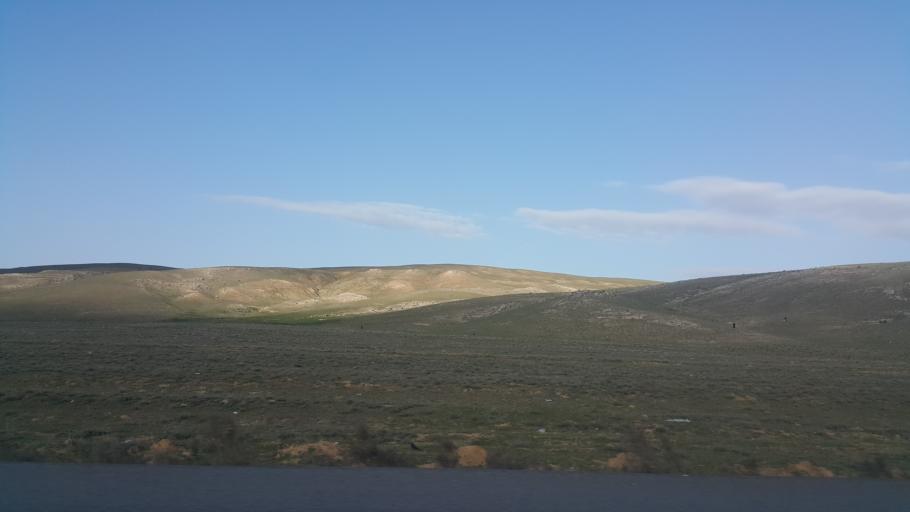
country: TR
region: Konya
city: Kulu
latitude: 39.1298
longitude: 33.3441
